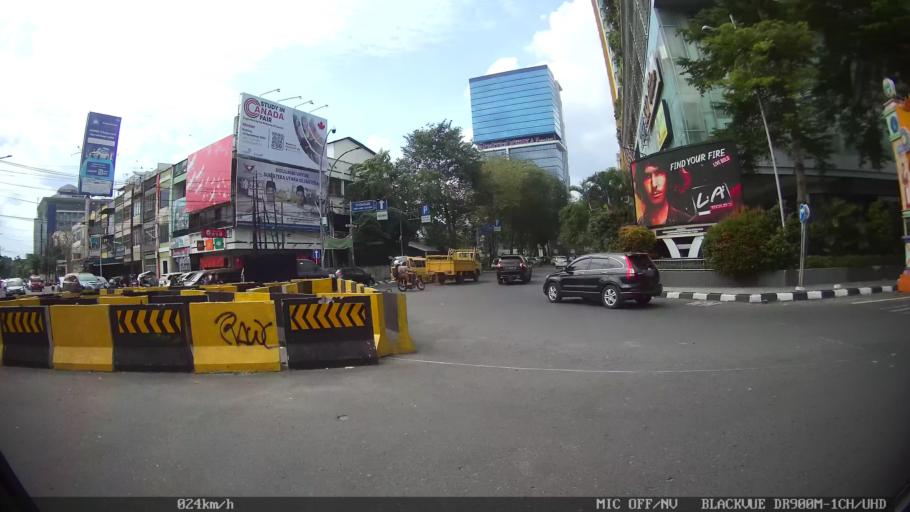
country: ID
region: North Sumatra
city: Medan
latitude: 3.5844
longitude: 98.6678
